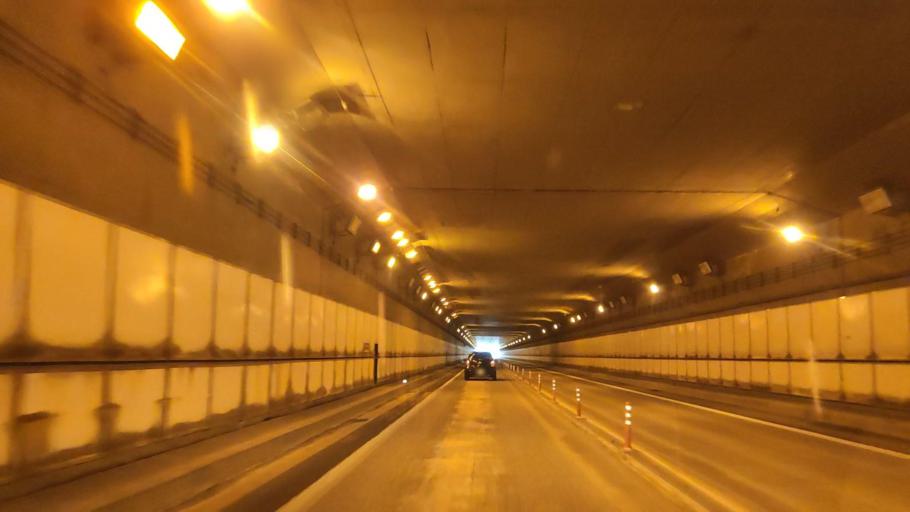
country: JP
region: Akita
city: Odate
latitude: 40.2763
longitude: 140.5349
